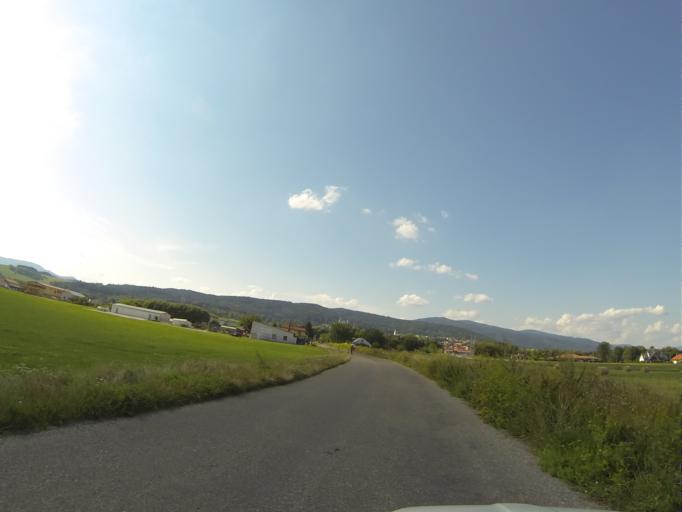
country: SK
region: Nitriansky
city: Bojnice
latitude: 48.7702
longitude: 18.5924
